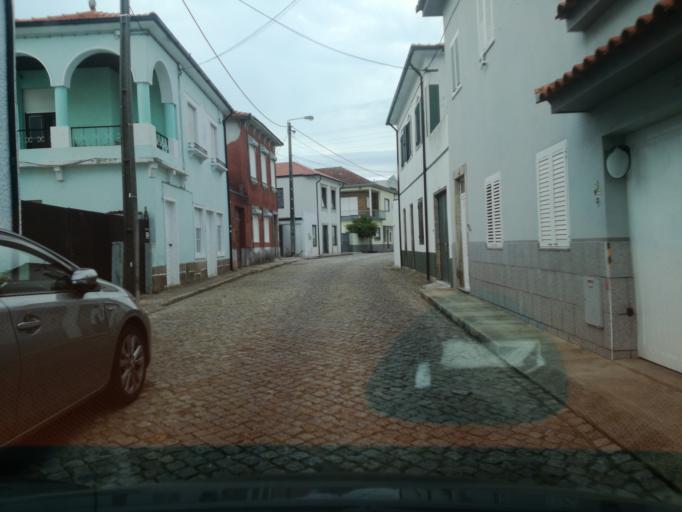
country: PT
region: Porto
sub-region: Maia
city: Maia
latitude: 41.2333
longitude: -8.6096
